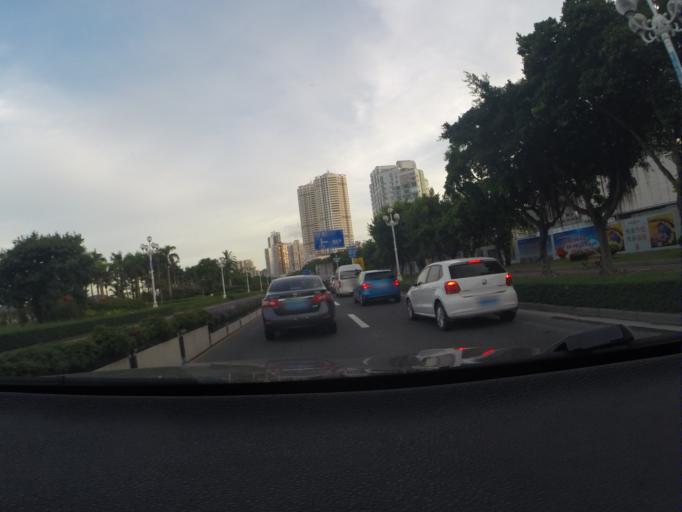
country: CN
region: Guangdong
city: Zhuhai
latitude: 22.2967
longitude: 113.5730
